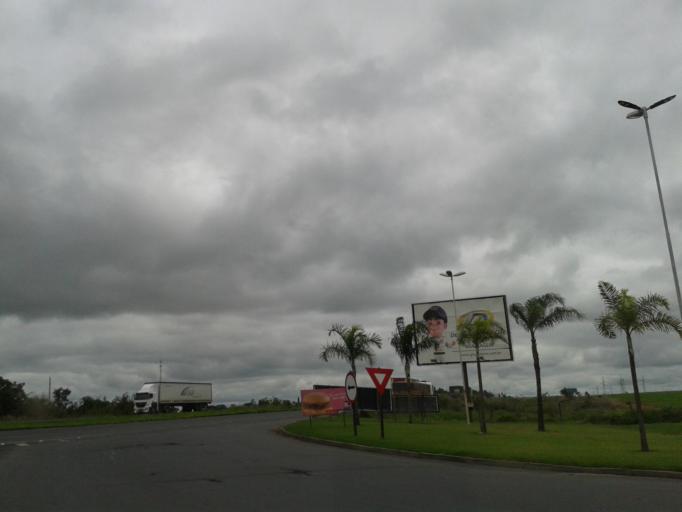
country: BR
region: Minas Gerais
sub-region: Uberlandia
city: Uberlandia
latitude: -19.0151
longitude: -48.2074
